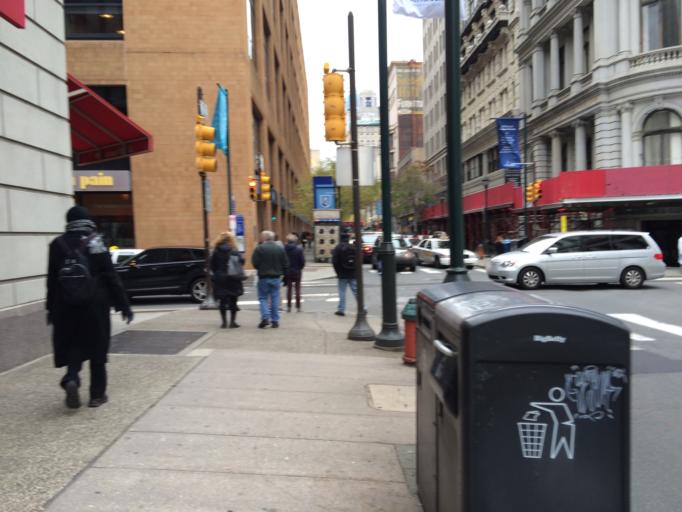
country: US
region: Pennsylvania
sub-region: Philadelphia County
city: Philadelphia
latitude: 39.9501
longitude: -75.1567
